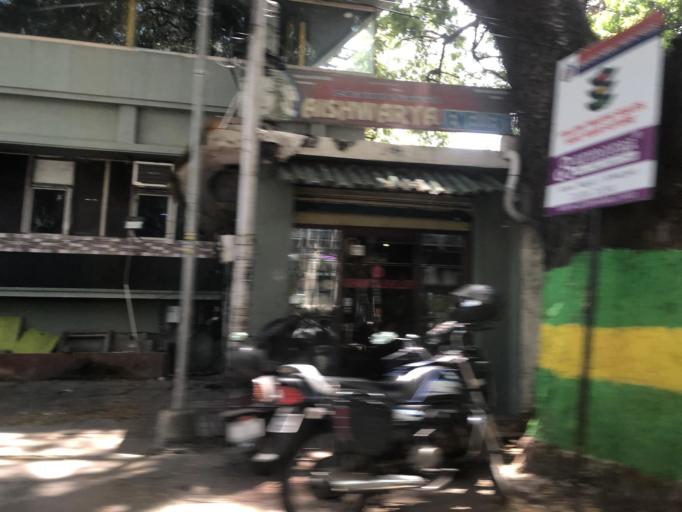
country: IN
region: Tamil Nadu
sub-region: Chennai
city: Chetput
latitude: 13.0423
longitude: 80.2591
